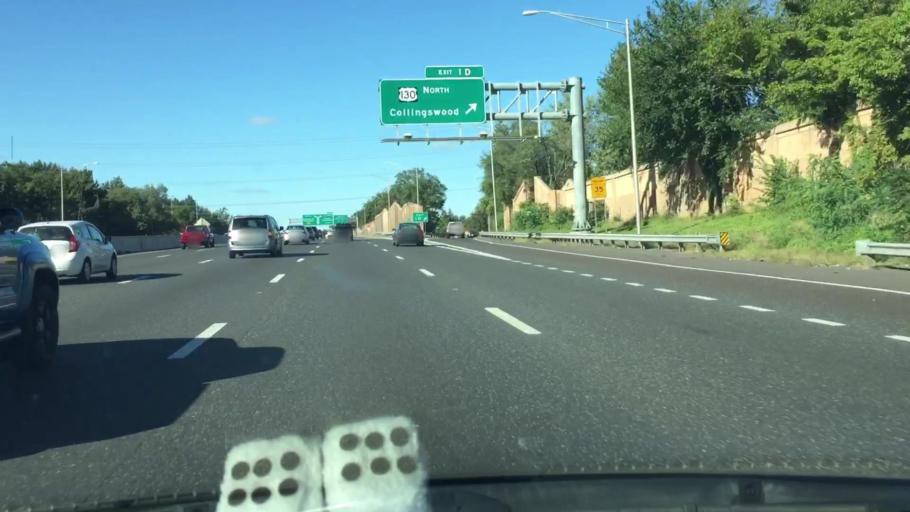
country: US
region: New Jersey
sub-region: Camden County
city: Mount Ephraim
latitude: 39.8845
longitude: -75.1035
